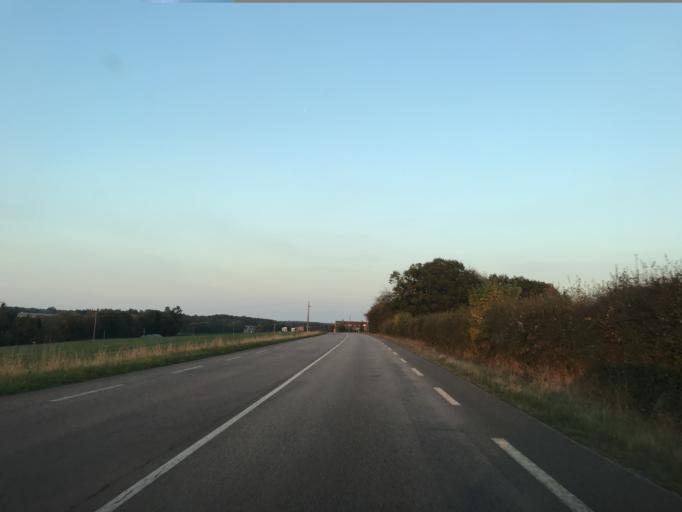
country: FR
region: Haute-Normandie
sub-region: Departement de l'Eure
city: Bourth
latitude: 48.6914
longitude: 0.8204
